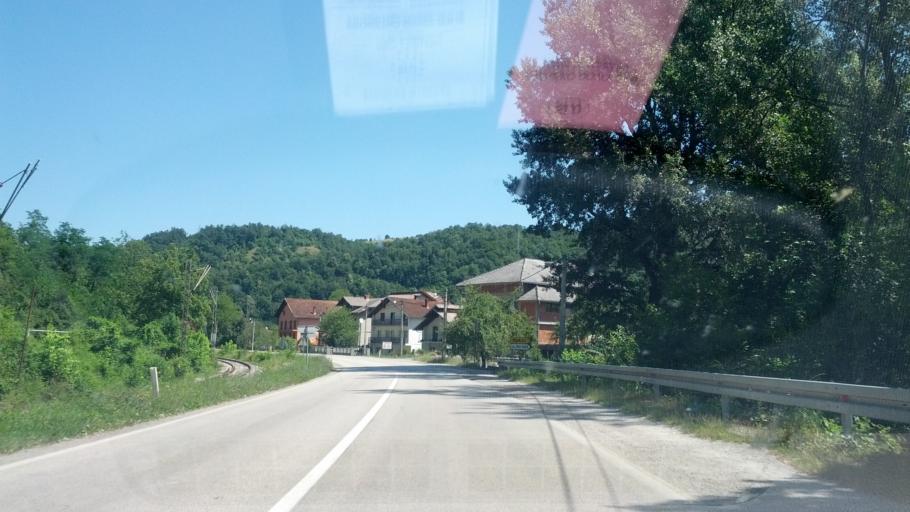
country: BA
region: Federation of Bosnia and Herzegovina
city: Bosanska Krupa
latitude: 44.9011
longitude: 16.1627
